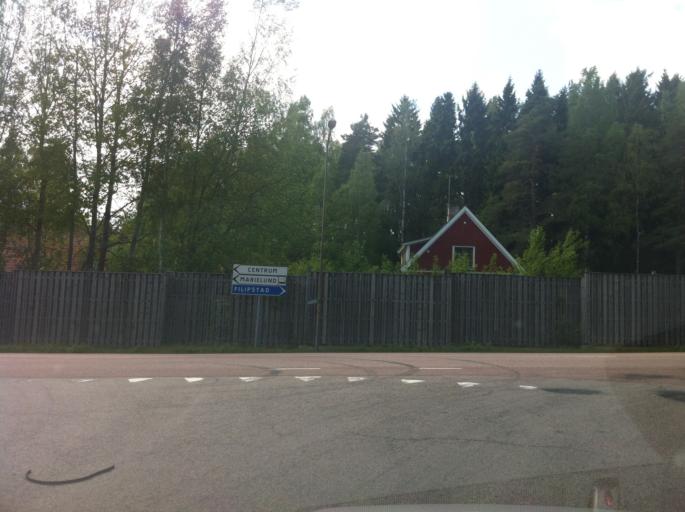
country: SE
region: Vaermland
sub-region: Kristinehamns Kommun
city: Kristinehamn
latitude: 59.3208
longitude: 14.1368
